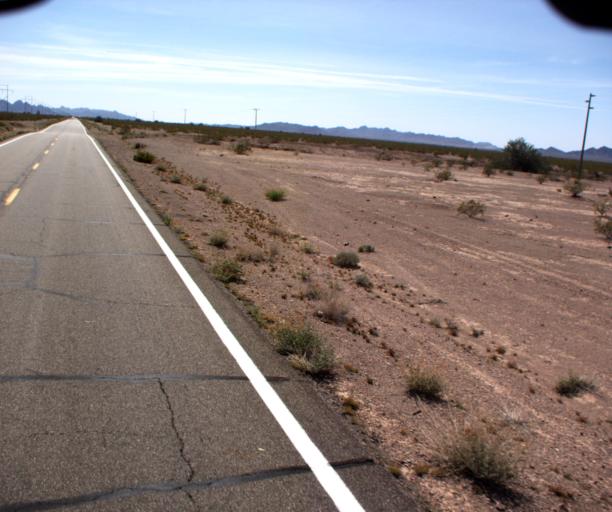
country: US
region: Arizona
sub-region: La Paz County
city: Quartzsite
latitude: 33.4269
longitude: -114.2170
